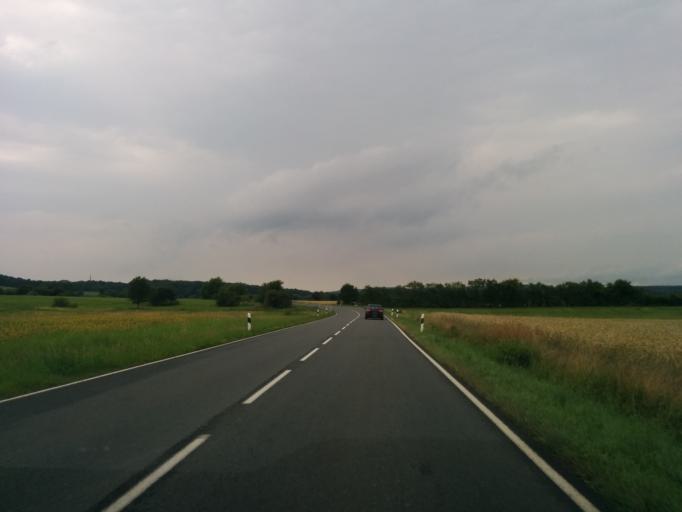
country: DE
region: Lower Saxony
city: Waake
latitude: 51.5848
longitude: 10.0615
